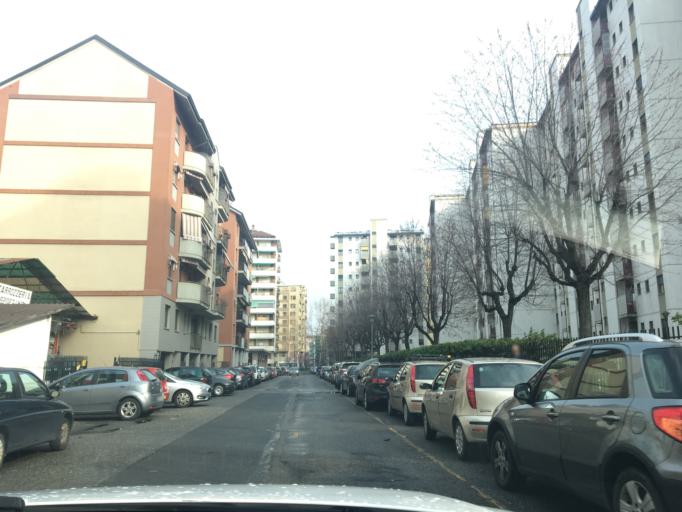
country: IT
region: Piedmont
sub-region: Provincia di Torino
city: Lesna
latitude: 45.0350
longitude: 7.6457
